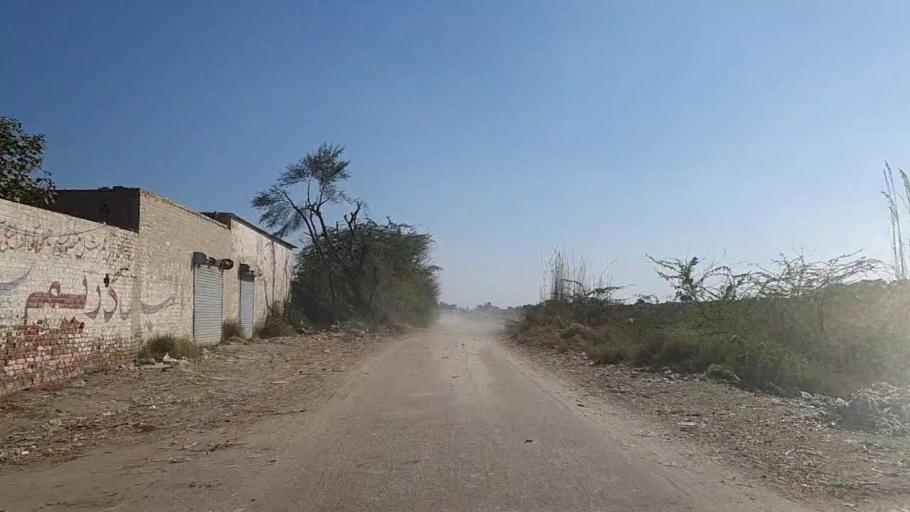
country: PK
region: Sindh
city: Nawabshah
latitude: 26.2385
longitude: 68.4245
